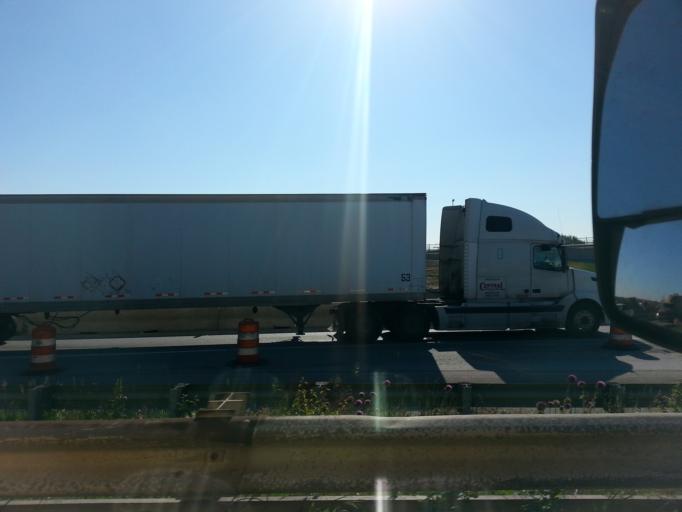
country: US
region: Indiana
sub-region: Clark County
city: Jeffersonville
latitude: 38.2769
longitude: -85.7497
